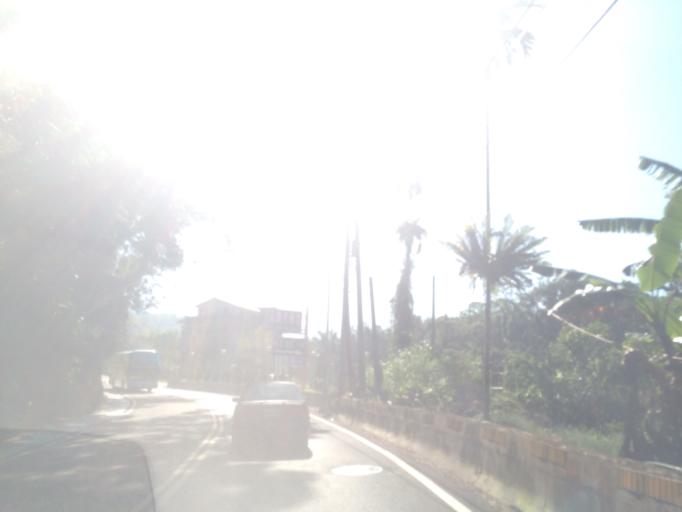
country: TW
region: Taiwan
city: Lugu
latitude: 23.7261
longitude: 120.7757
